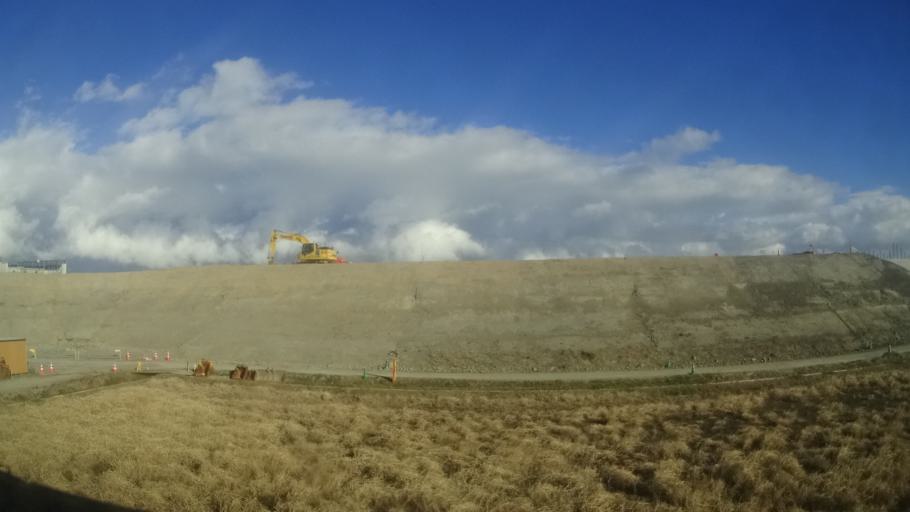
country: JP
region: Miyagi
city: Marumori
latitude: 37.8759
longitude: 140.9269
